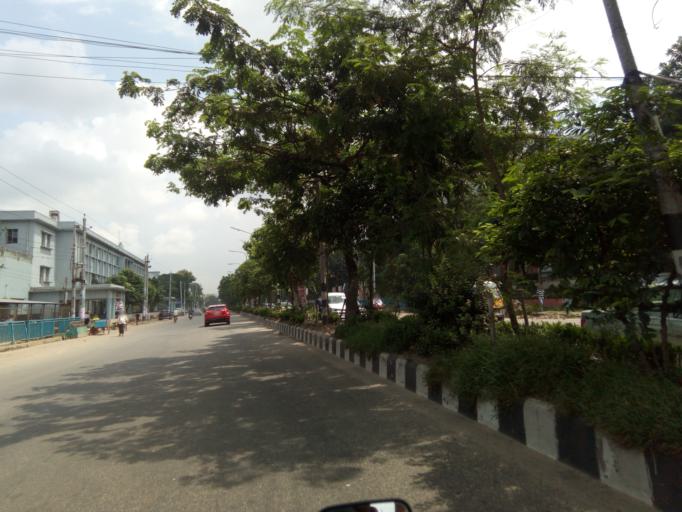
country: BD
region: Dhaka
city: Paltan
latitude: 23.7597
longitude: 90.3994
